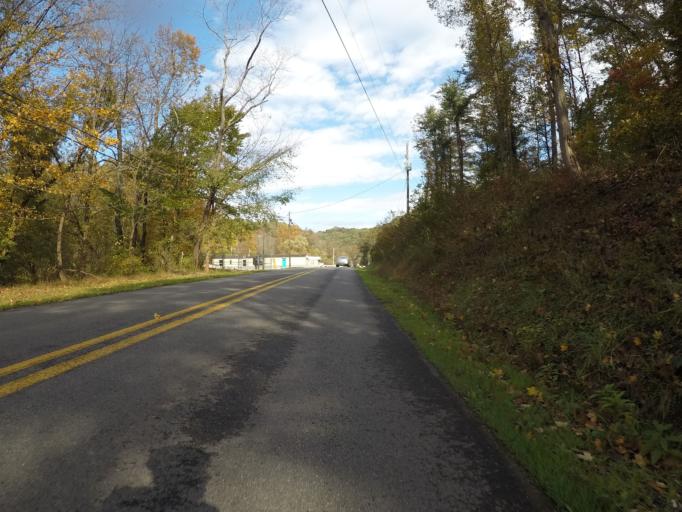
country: US
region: West Virginia
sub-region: Wayne County
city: Lavalette
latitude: 38.3537
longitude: -82.4371
